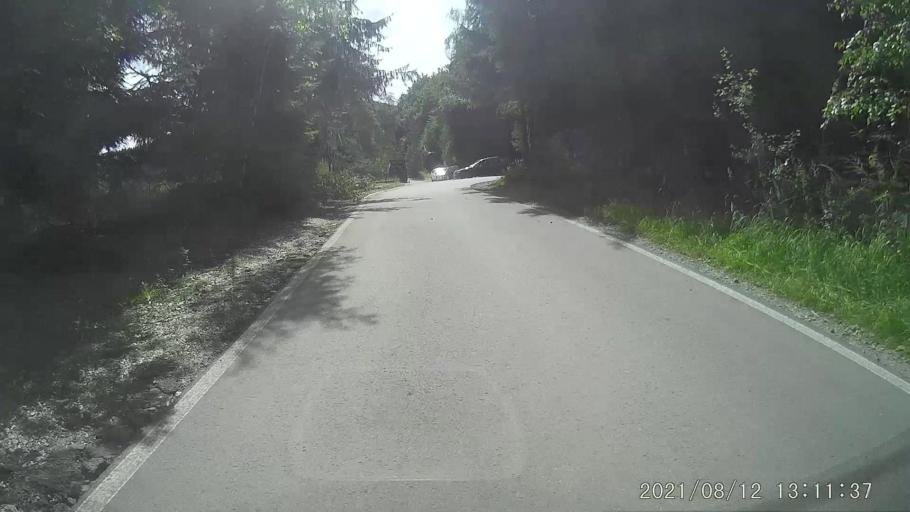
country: PL
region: Lower Silesian Voivodeship
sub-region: Powiat klodzki
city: Stronie Slaskie
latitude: 50.2434
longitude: 16.8517
